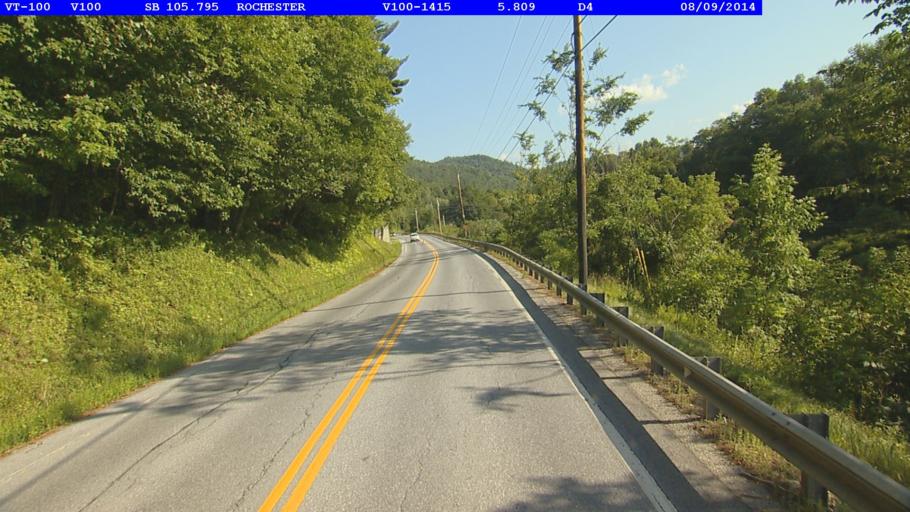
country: US
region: Vermont
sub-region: Orange County
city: Randolph
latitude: 43.8815
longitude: -72.8084
